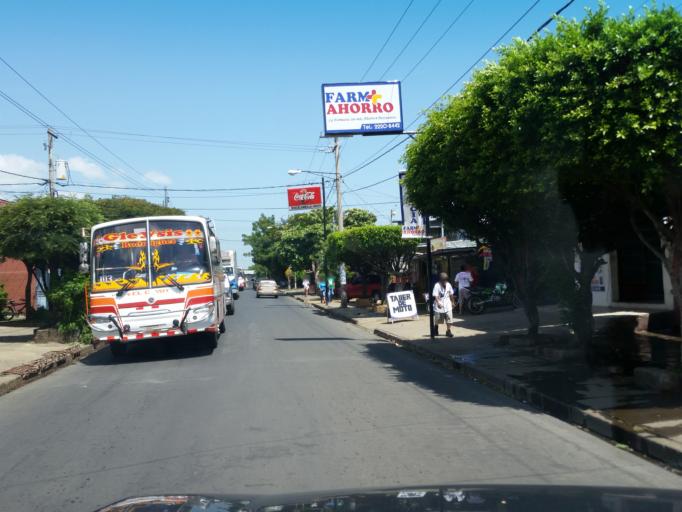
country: NI
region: Managua
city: Managua
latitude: 12.1194
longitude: -86.2072
